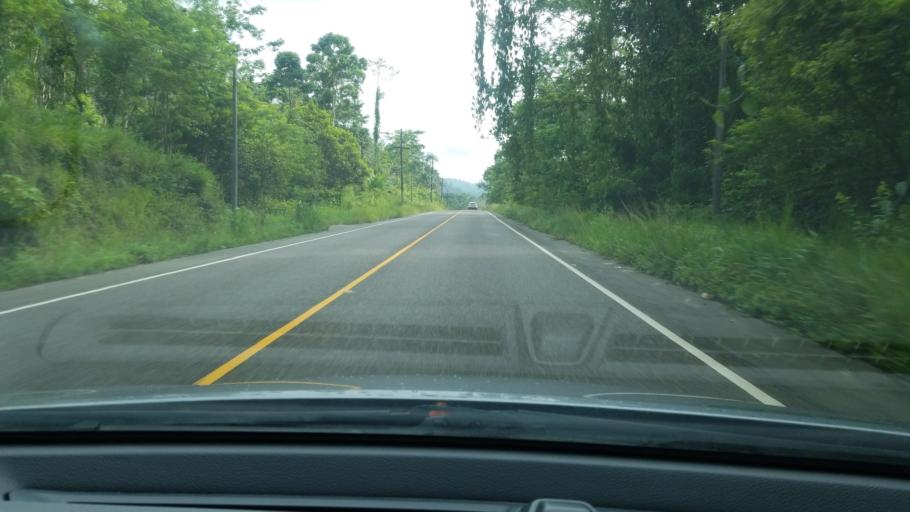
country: HN
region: Cortes
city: Potrerillos
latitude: 15.6049
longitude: -88.2931
